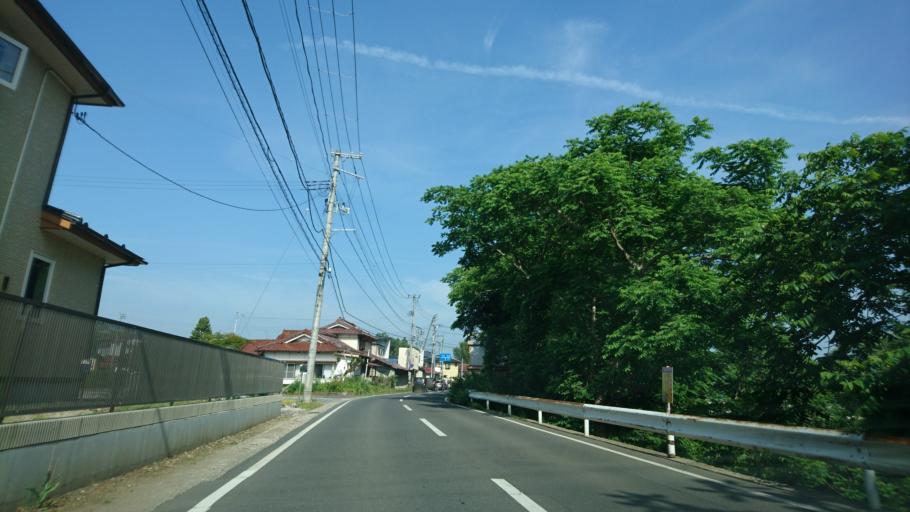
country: JP
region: Iwate
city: Ichinoseki
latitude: 38.9235
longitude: 141.1181
